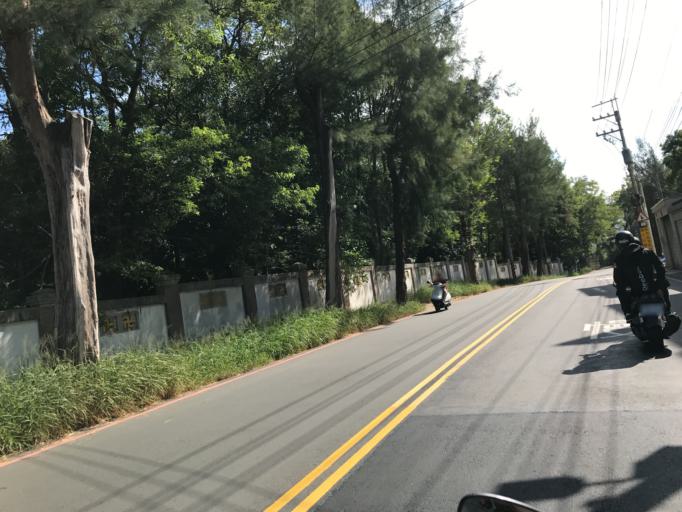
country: TW
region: Taiwan
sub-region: Hsinchu
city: Hsinchu
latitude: 24.7711
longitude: 120.9726
